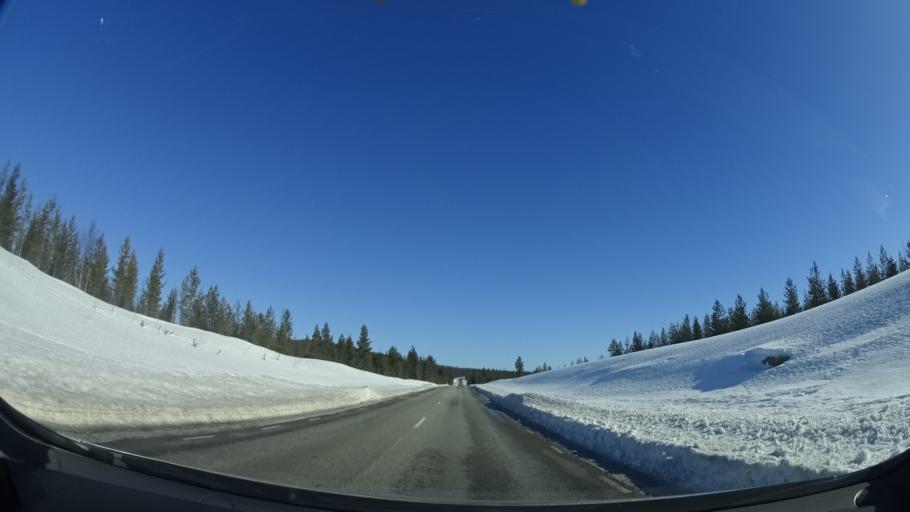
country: SE
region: Vaesterbotten
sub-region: Skelleftea Kommun
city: Langsele
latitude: 65.1168
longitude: 20.0929
